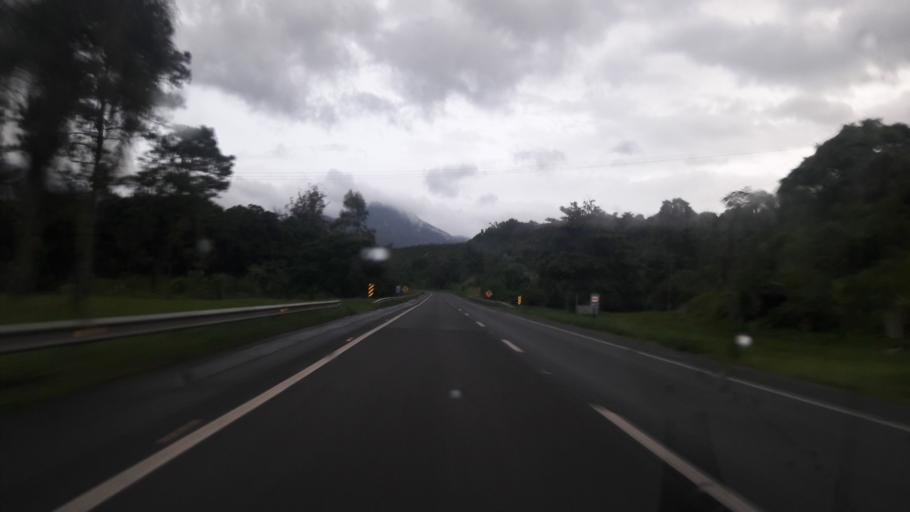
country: BR
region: Sao Paulo
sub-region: Cajati
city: Cajati
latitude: -24.7811
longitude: -48.1920
